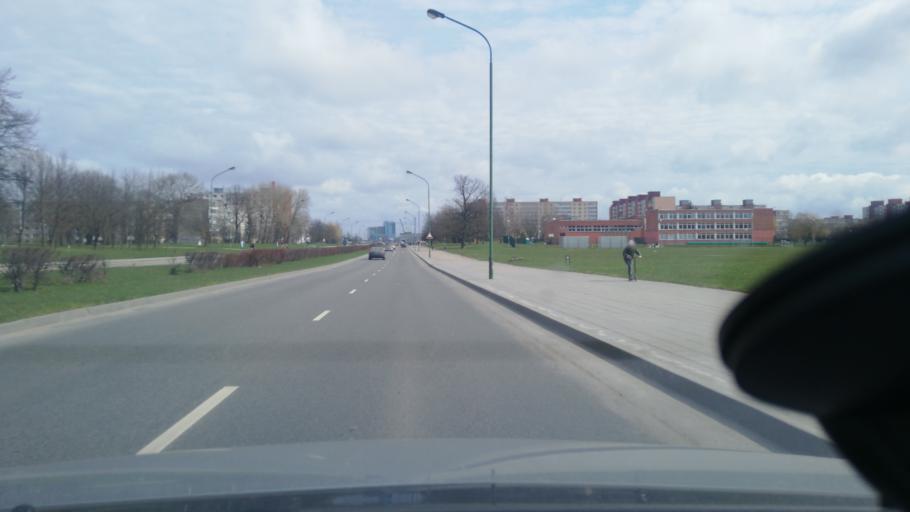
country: LT
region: Klaipedos apskritis
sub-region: Klaipeda
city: Klaipeda
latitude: 55.6750
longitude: 21.1807
